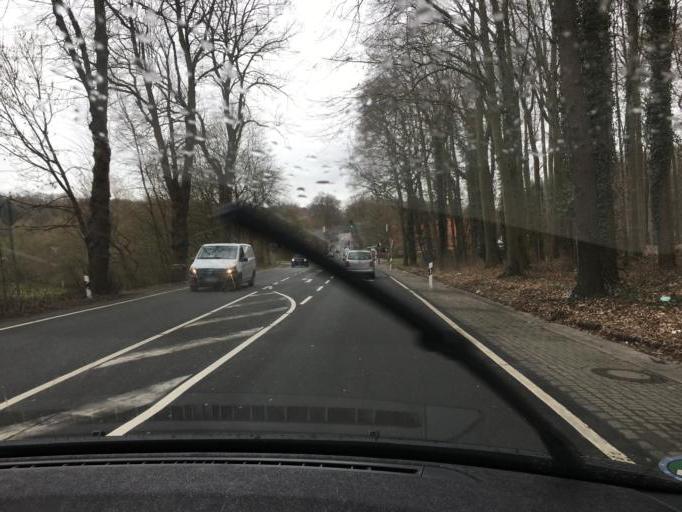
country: DE
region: North Rhine-Westphalia
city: Herdecke
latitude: 51.4306
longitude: 7.4669
